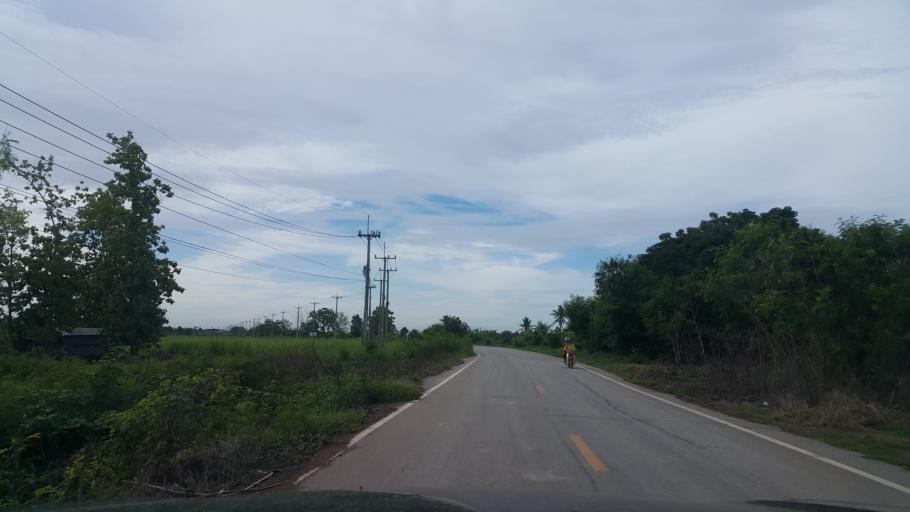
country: TH
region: Sukhothai
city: Si Nakhon
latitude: 17.2781
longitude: 99.9757
